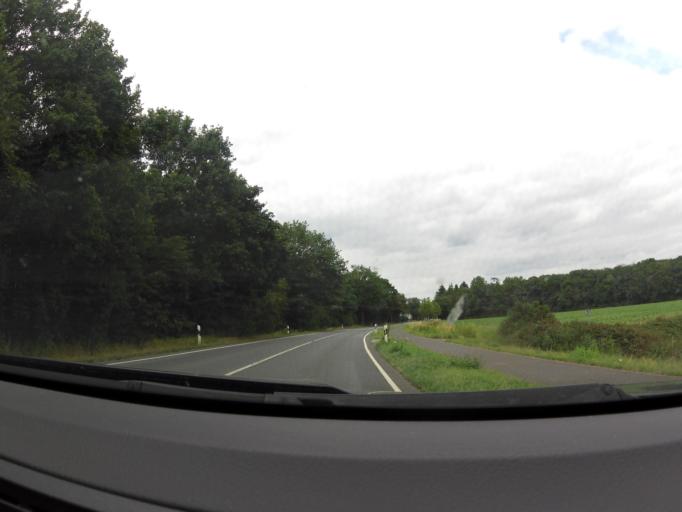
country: DE
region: North Rhine-Westphalia
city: Geldern
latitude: 51.5404
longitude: 6.3139
